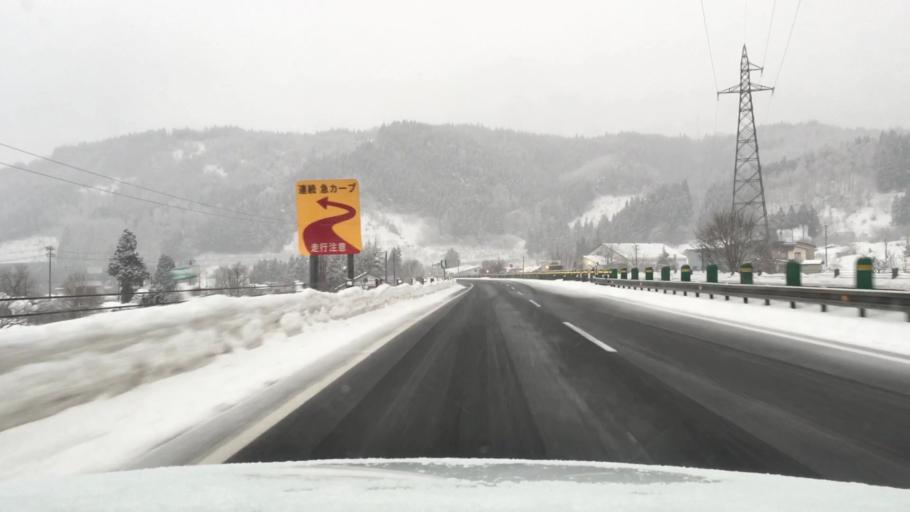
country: JP
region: Aomori
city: Kuroishi
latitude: 40.5245
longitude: 140.5819
